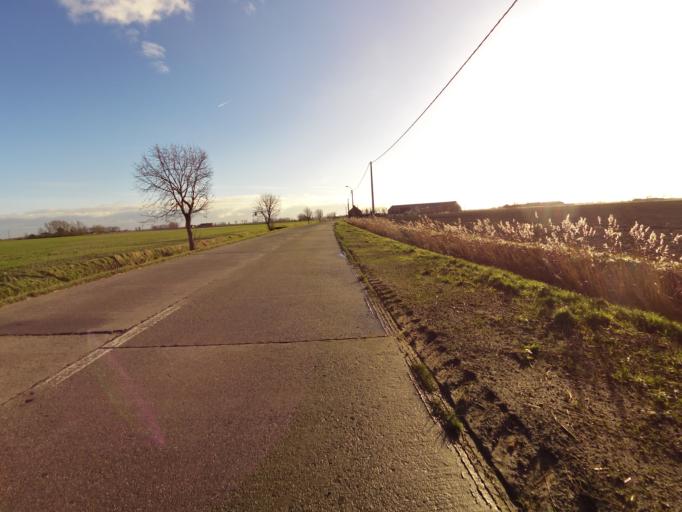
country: BE
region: Flanders
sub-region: Provincie West-Vlaanderen
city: Middelkerke
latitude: 51.1642
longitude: 2.8829
